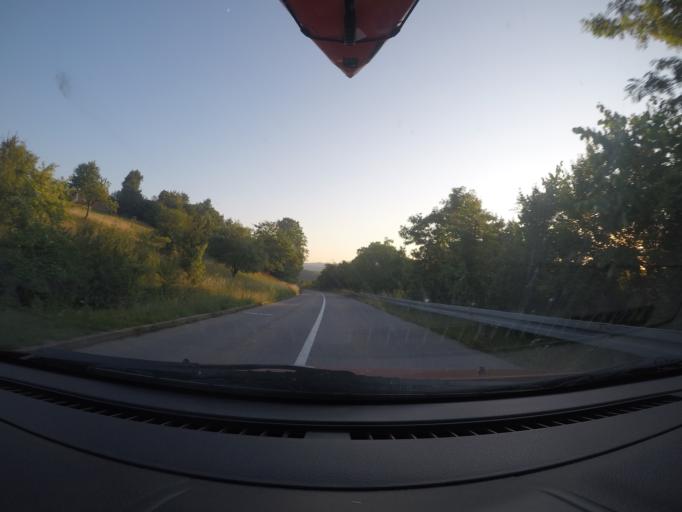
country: RO
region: Mehedinti
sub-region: Comuna Dubova
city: Dubova
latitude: 44.6544
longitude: 22.3129
